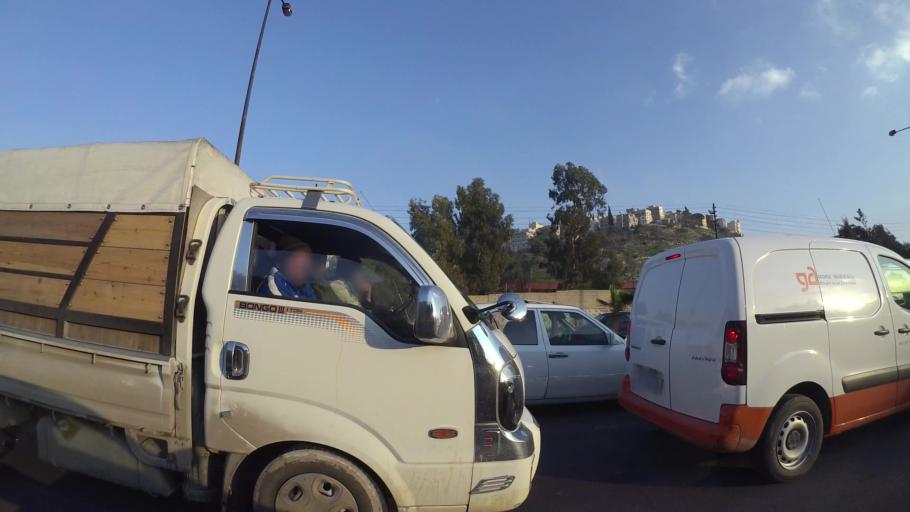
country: JO
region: Amman
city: Amman
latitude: 31.9808
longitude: 35.9736
